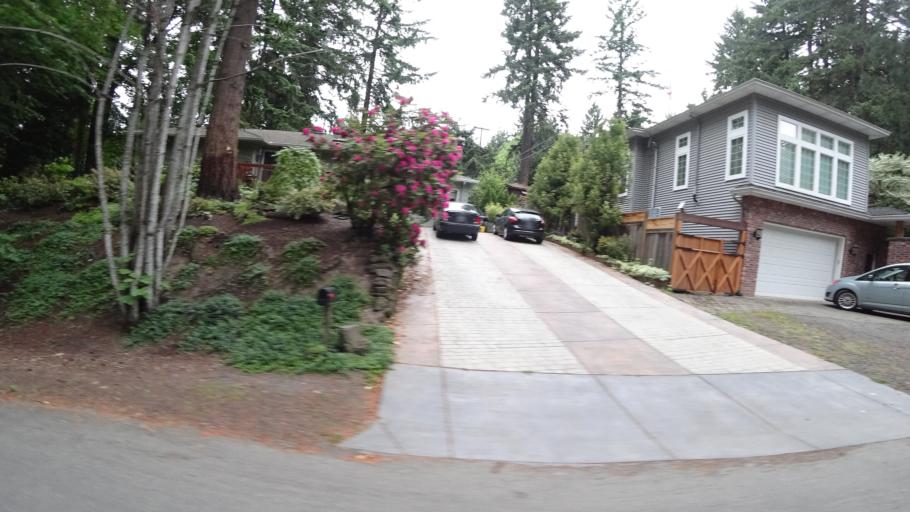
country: US
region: Oregon
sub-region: Multnomah County
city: Portland
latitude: 45.4849
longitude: -122.7008
